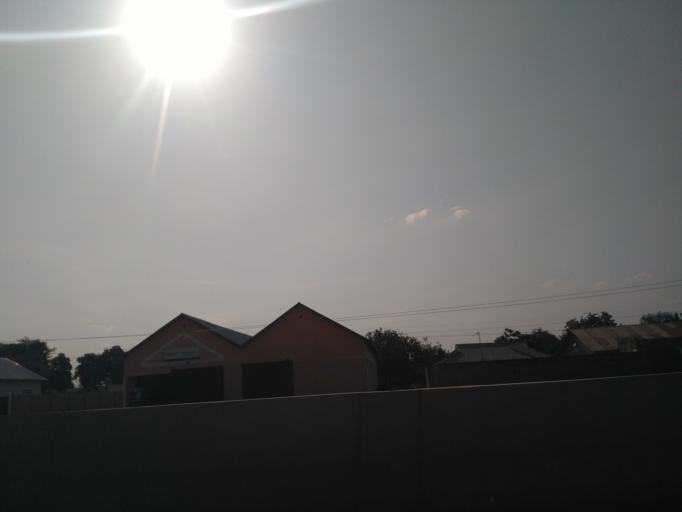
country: TZ
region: Dar es Salaam
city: Dar es Salaam
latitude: -6.8554
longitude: 39.3105
